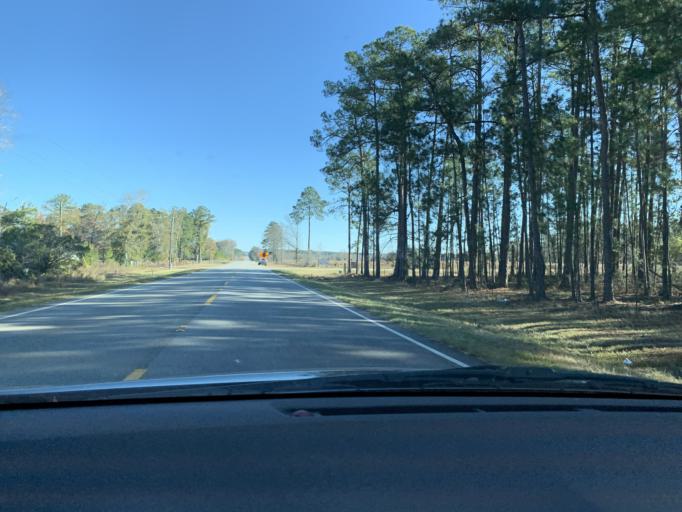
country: US
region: Georgia
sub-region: Ben Hill County
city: Fitzgerald
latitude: 31.7495
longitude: -83.1387
